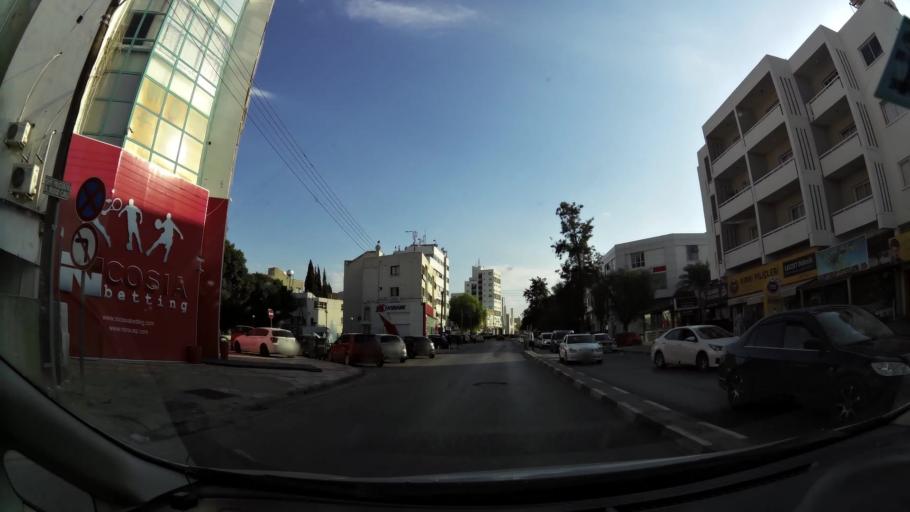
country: CY
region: Lefkosia
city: Nicosia
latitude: 35.1917
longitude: 33.3673
